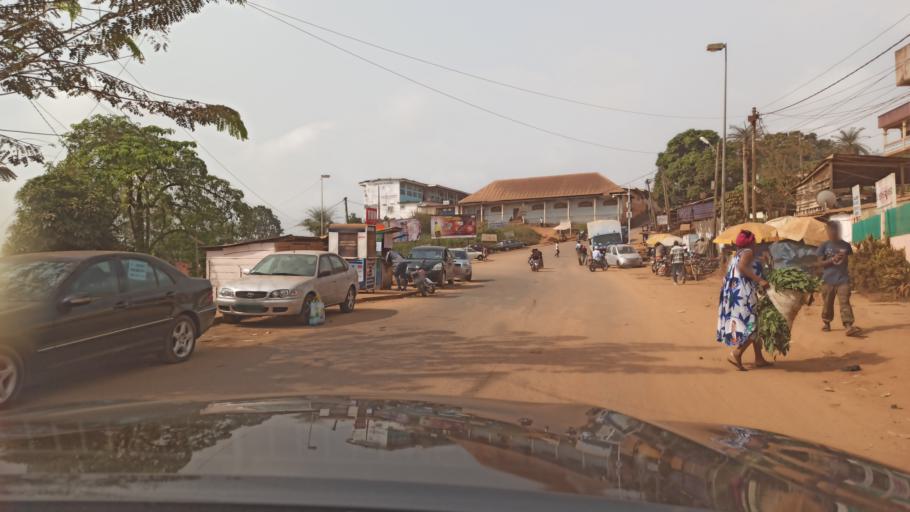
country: CM
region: Centre
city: Yaounde
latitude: 3.8772
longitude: 11.4844
